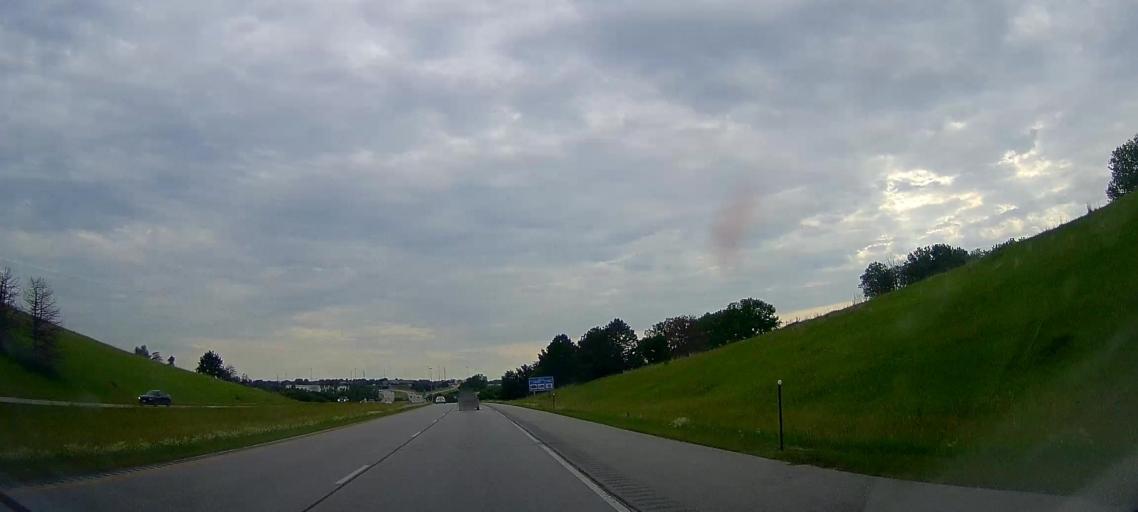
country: US
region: Nebraska
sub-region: Douglas County
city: Bennington
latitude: 41.3295
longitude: -96.0586
